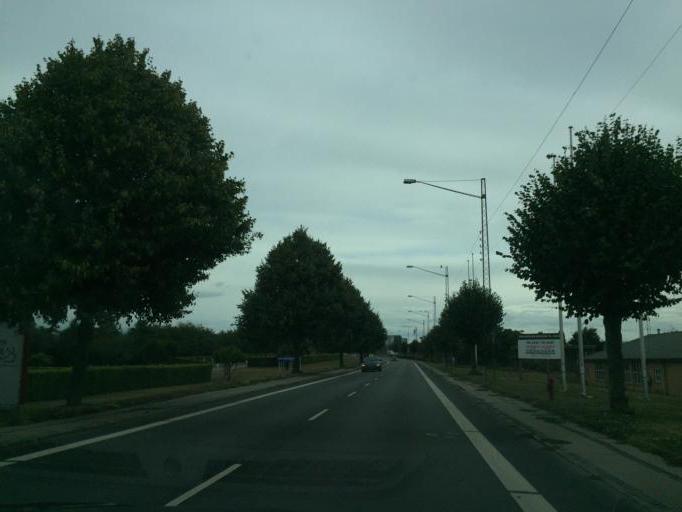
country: DK
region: South Denmark
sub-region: Middelfart Kommune
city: Middelfart
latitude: 55.5044
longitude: 9.7574
